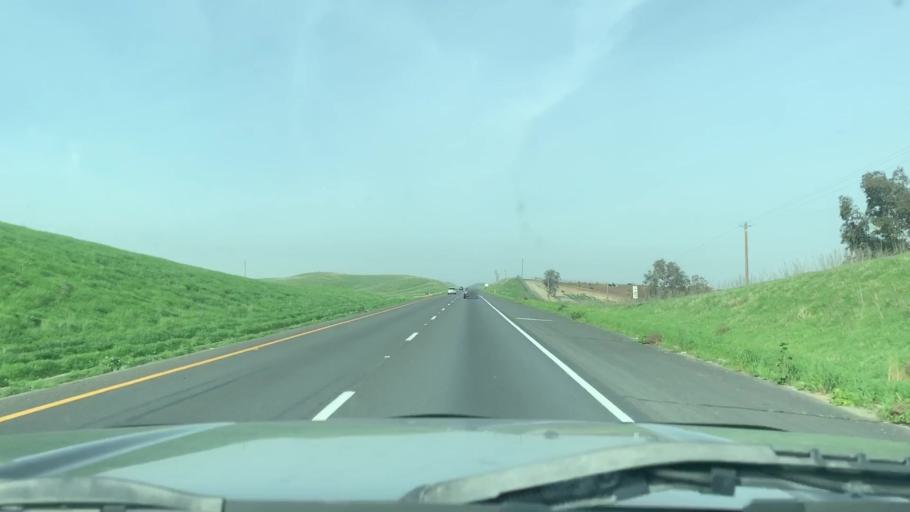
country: US
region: California
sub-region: Fresno County
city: Coalinga
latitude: 36.3070
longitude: -120.2786
